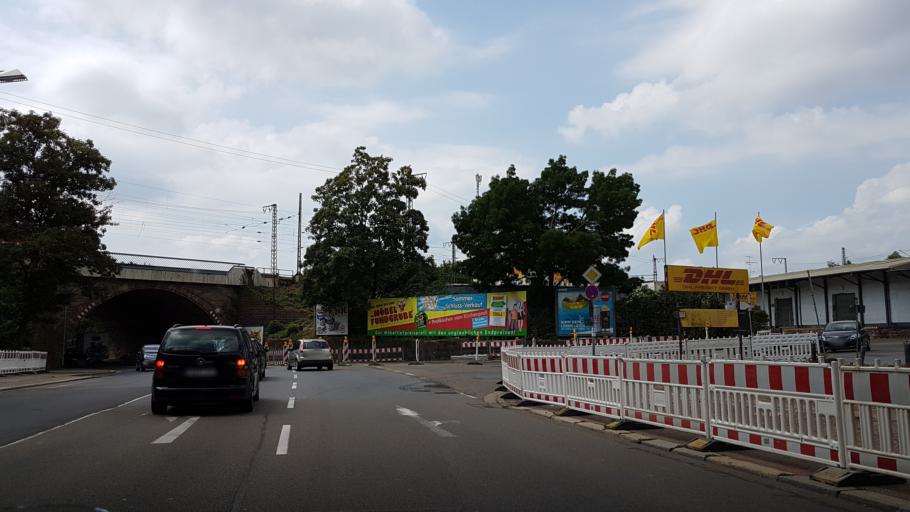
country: DE
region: Saarland
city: Saarbrucken
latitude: 49.2426
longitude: 7.0022
